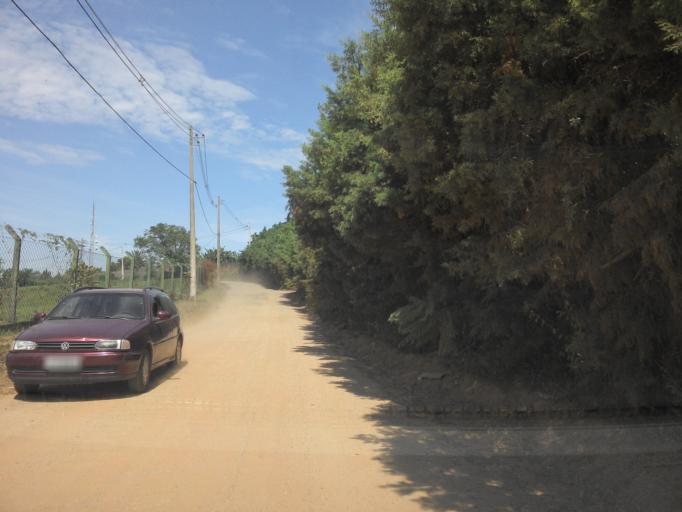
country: BR
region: Sao Paulo
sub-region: Valinhos
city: Valinhos
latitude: -22.9333
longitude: -46.9877
